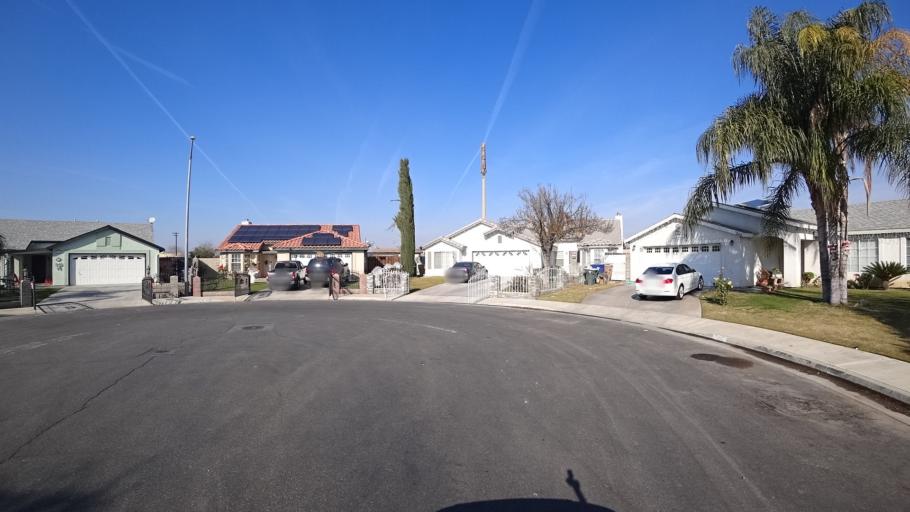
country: US
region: California
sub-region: Kern County
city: Greenfield
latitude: 35.3159
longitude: -119.0257
